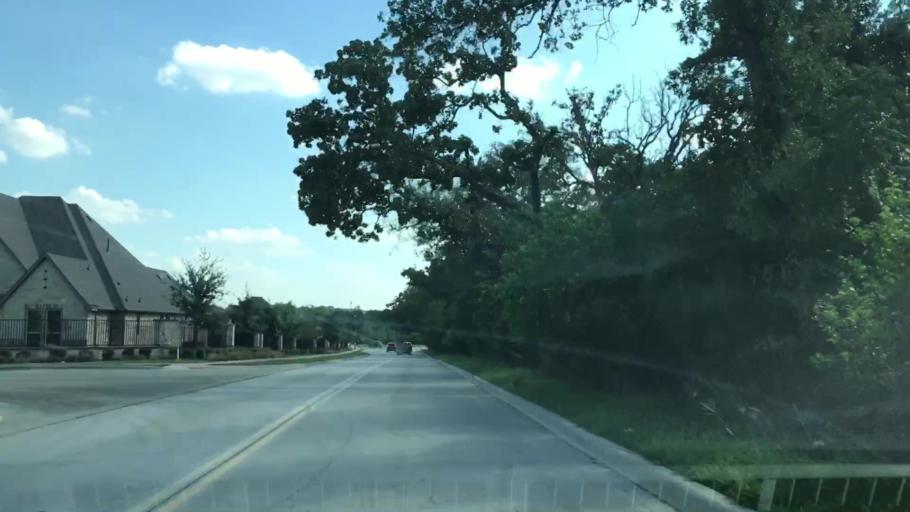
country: US
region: Texas
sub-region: Tarrant County
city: Keller
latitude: 32.9021
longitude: -97.2202
